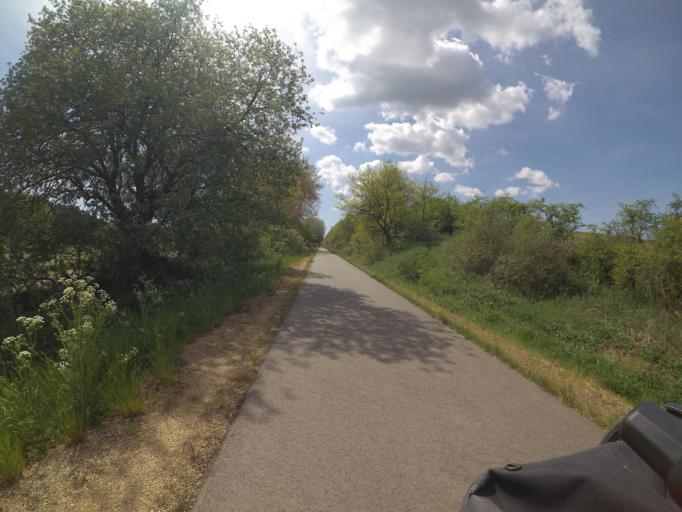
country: BE
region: Wallonia
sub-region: Province de Liege
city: Bullange
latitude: 50.4010
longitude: 6.2686
